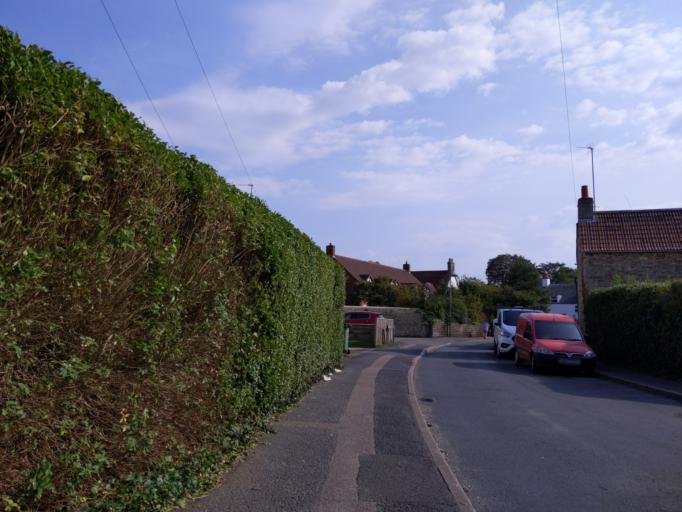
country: GB
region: England
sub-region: Oxfordshire
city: Cowley
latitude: 51.7212
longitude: -1.2269
